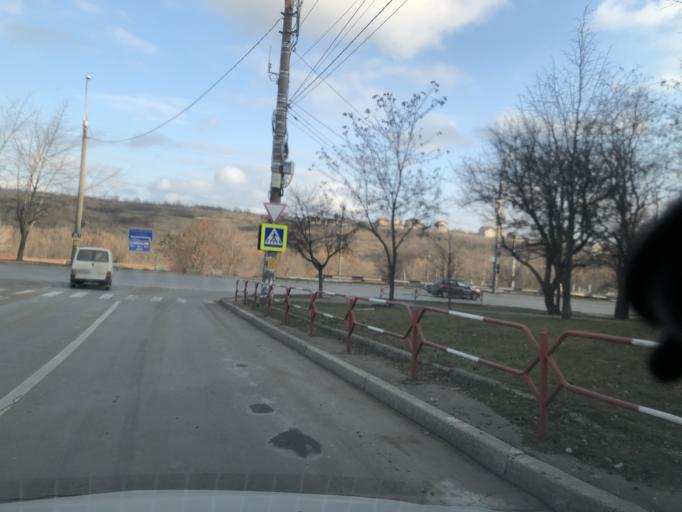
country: MD
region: Chisinau
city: Stauceni
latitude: 47.0565
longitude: 28.8971
